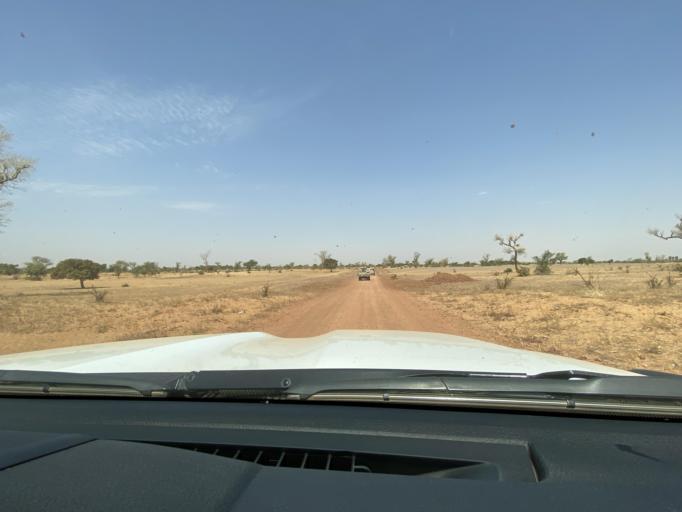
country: NE
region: Dosso
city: Birnin Gaoure
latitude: 13.2326
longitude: 2.8689
